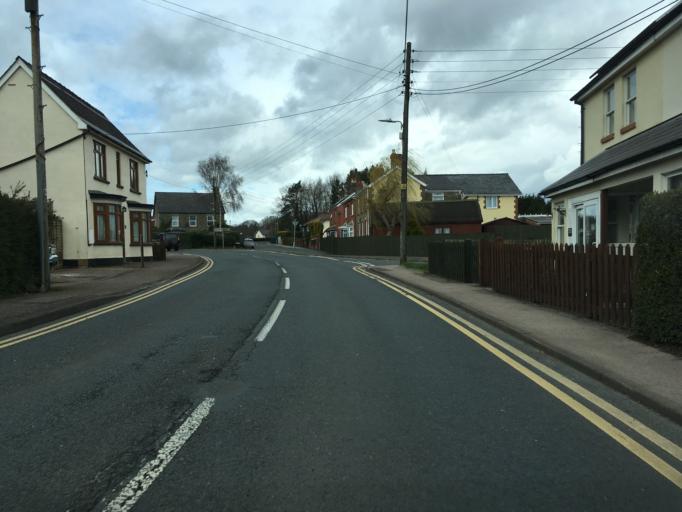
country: GB
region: England
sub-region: Gloucestershire
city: Coleford
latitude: 51.8026
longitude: -2.5981
